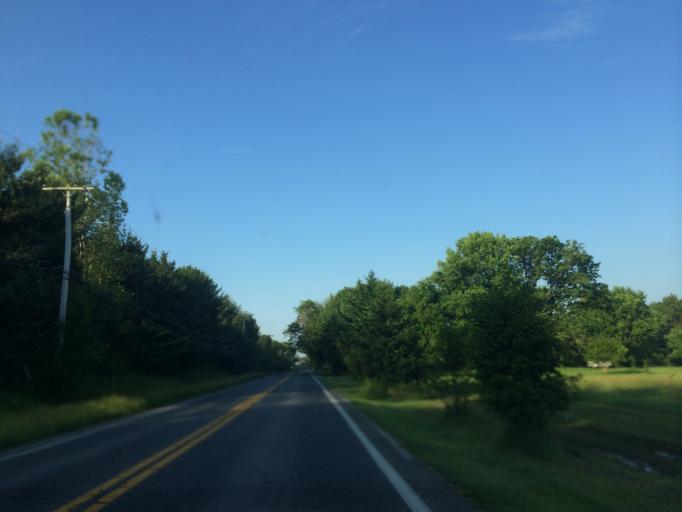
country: US
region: Maryland
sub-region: Howard County
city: Highland
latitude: 39.1805
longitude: -76.9331
